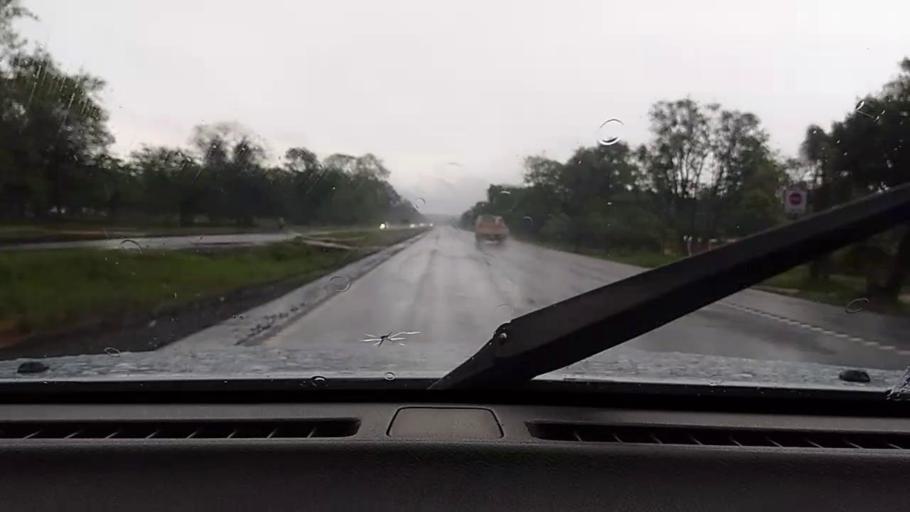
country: PY
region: Caaguazu
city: Repatriacion
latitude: -25.4569
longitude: -55.9168
